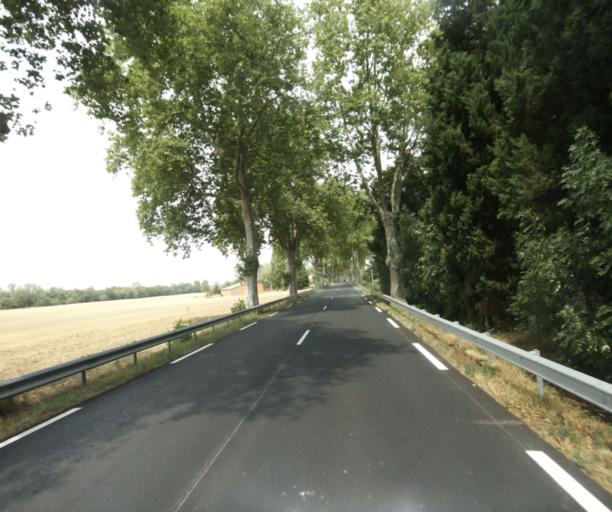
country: FR
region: Midi-Pyrenees
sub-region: Departement de la Haute-Garonne
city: Revel
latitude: 43.4396
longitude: 1.9523
